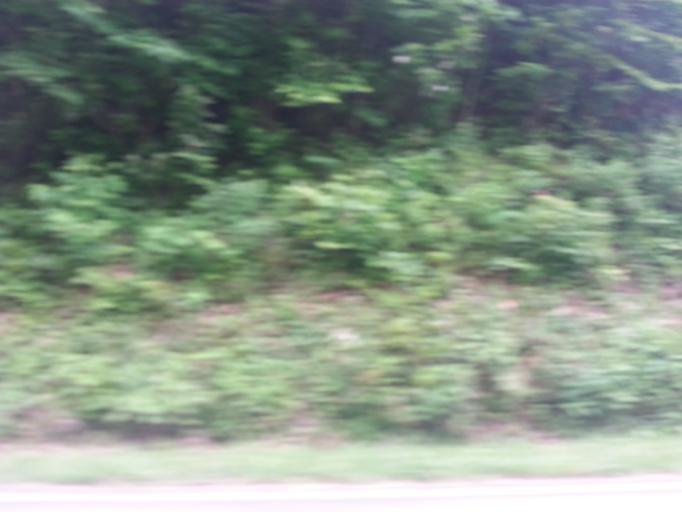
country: US
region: Georgia
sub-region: Towns County
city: Hiawassee
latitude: 34.8530
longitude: -83.7999
